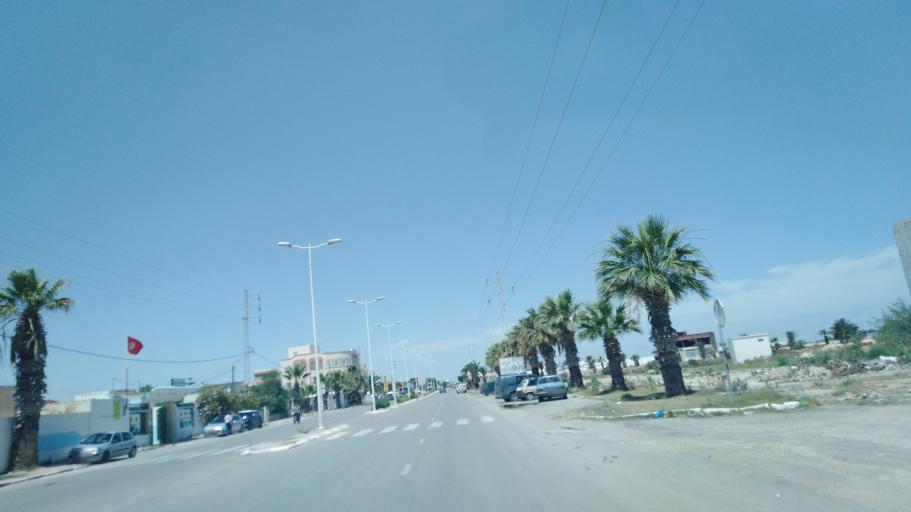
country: TN
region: Al Mahdiyah
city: Ksour Essaf
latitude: 35.4249
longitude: 10.9954
